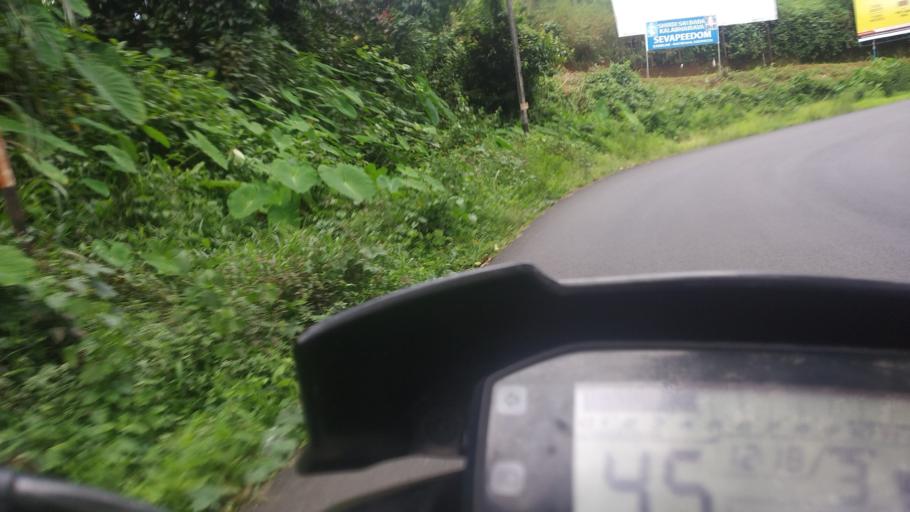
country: IN
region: Kerala
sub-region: Idukki
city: Munnar
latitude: 10.0179
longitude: 77.0066
